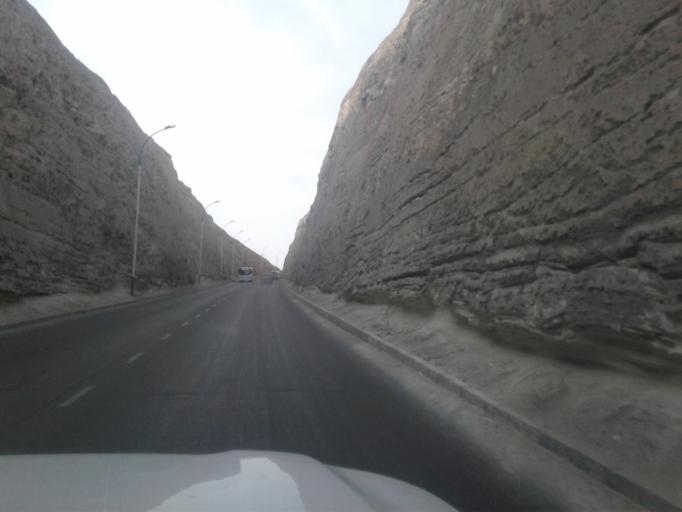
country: TM
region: Balkan
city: Turkmenbasy
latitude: 40.0379
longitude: 52.9705
